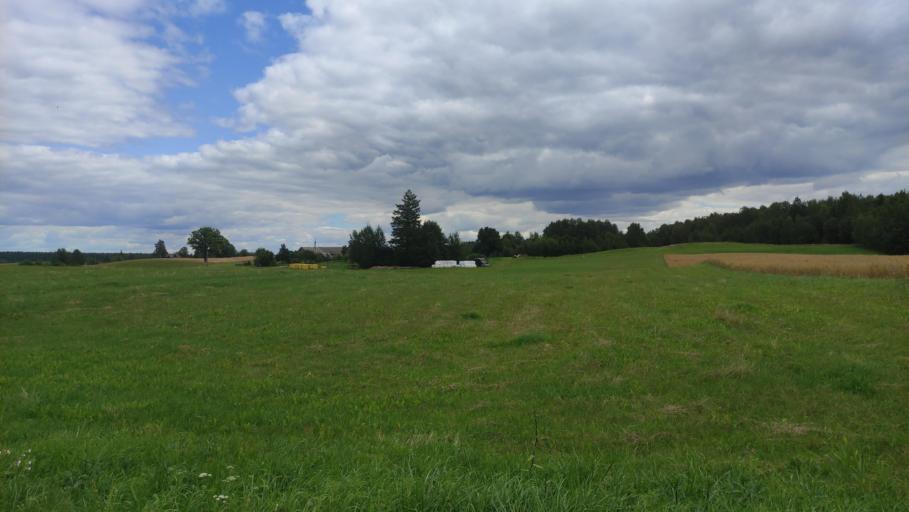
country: LT
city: Veisiejai
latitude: 54.1257
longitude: 23.6075
